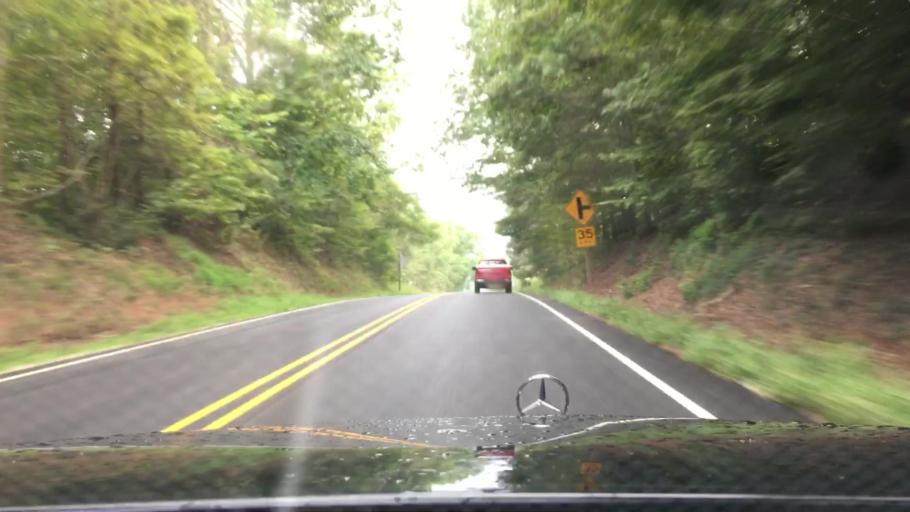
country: US
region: Virginia
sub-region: Nelson County
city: Nellysford
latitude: 37.9078
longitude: -78.8509
